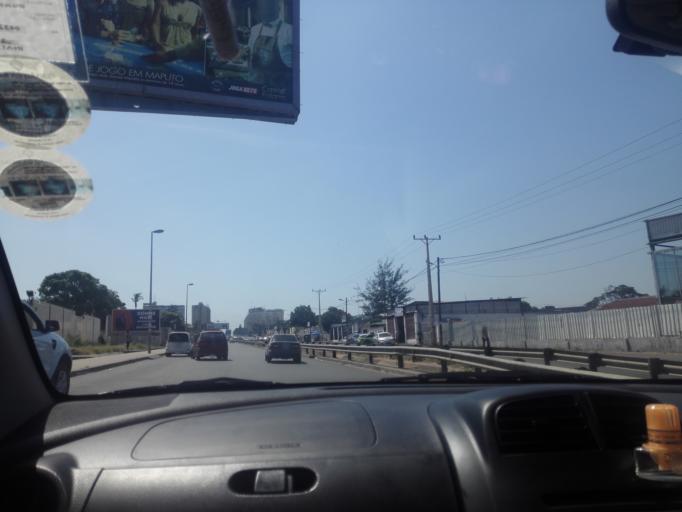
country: MZ
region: Maputo City
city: Maputo
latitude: -25.9487
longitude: 32.5824
